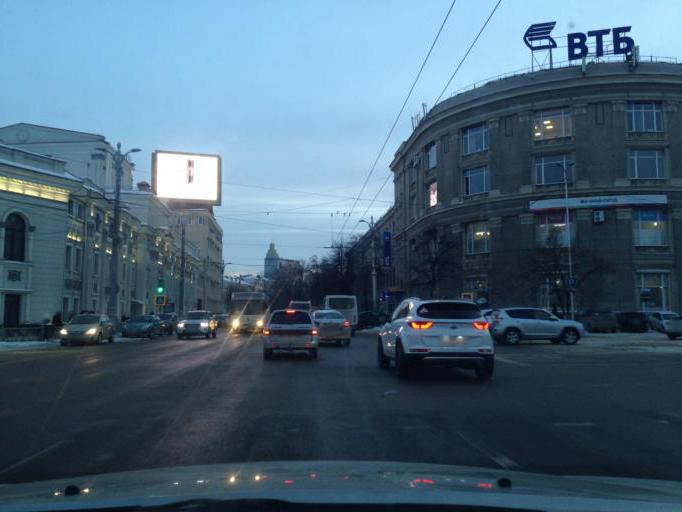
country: RU
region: Voronezj
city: Voronezh
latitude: 51.6645
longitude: 39.2047
